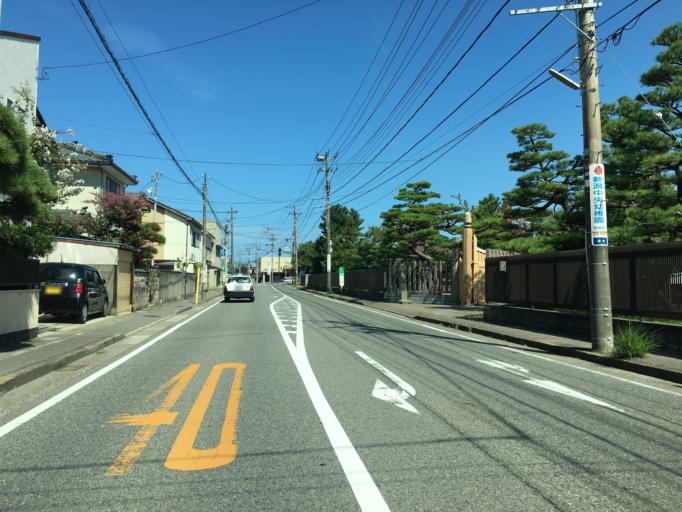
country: JP
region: Niigata
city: Niigata-shi
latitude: 37.9301
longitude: 139.0565
